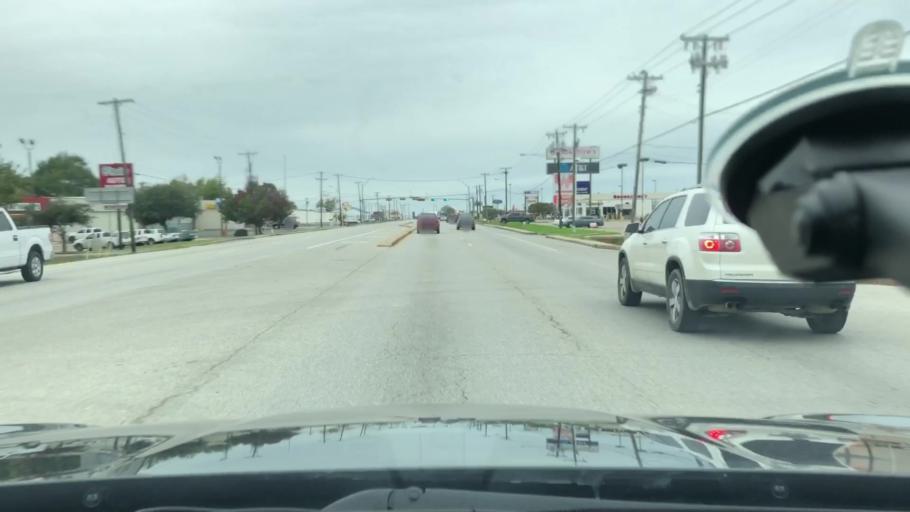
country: US
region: Texas
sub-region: Kaufman County
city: Terrell
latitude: 32.7383
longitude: -96.2964
